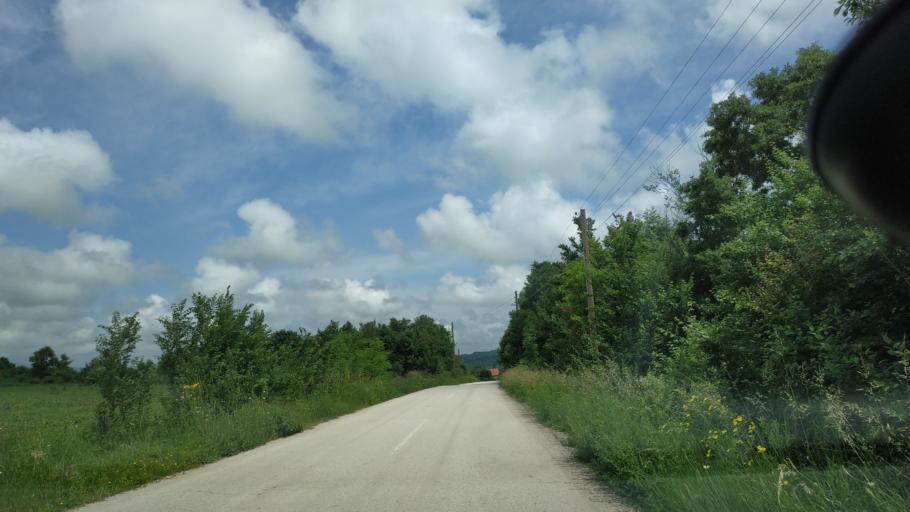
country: RS
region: Central Serbia
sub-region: Zajecarski Okrug
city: Boljevac
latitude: 43.8186
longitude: 21.9523
